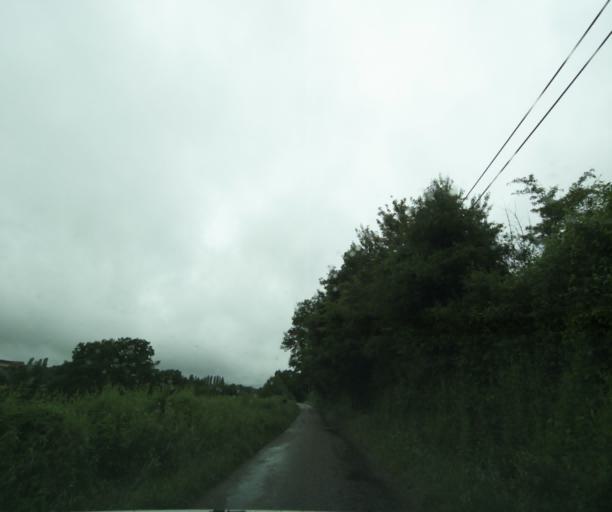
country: FR
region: Bourgogne
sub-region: Departement de Saone-et-Loire
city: Charolles
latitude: 46.4110
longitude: 4.3176
